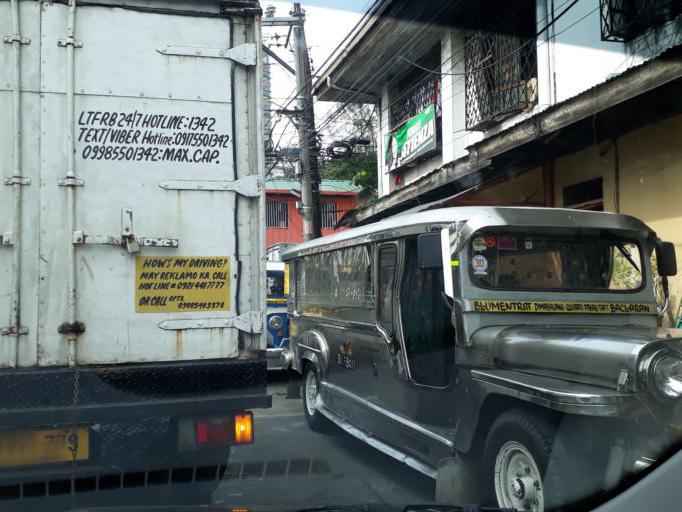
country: PH
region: Metro Manila
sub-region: City of Manila
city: Manila
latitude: 14.6234
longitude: 120.9883
